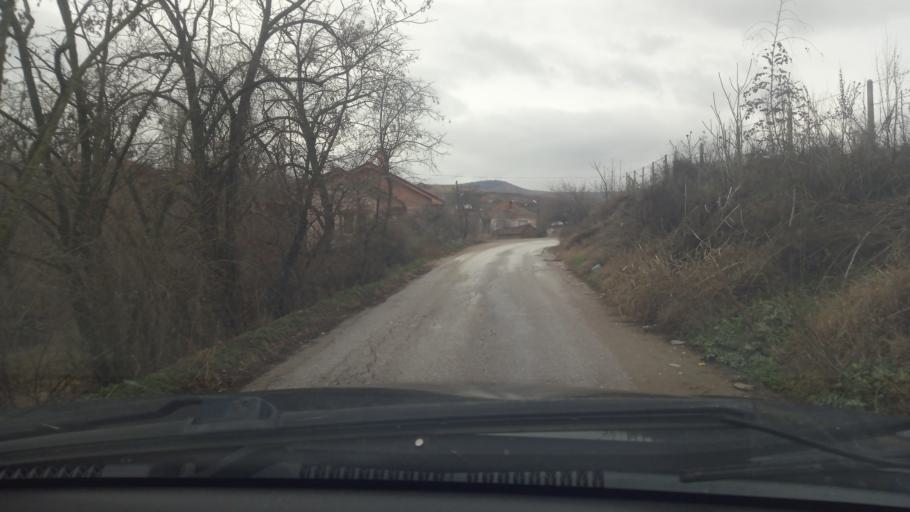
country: MK
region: Gradsko
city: Gradsko
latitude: 41.6006
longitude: 21.9007
